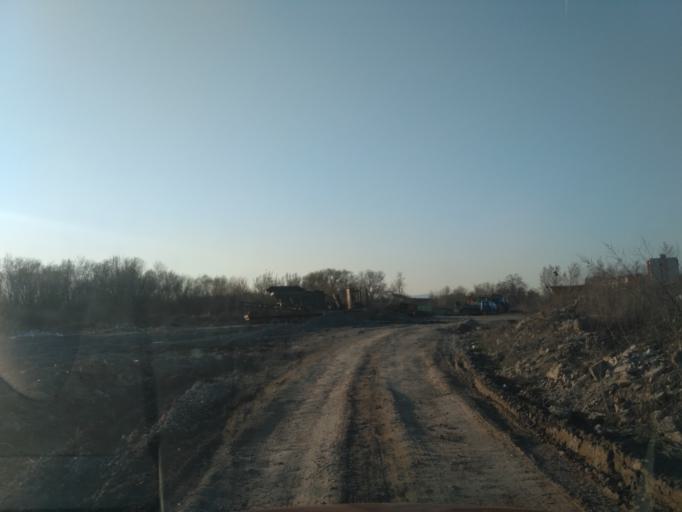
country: SK
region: Kosicky
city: Kosice
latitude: 48.6678
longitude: 21.3057
